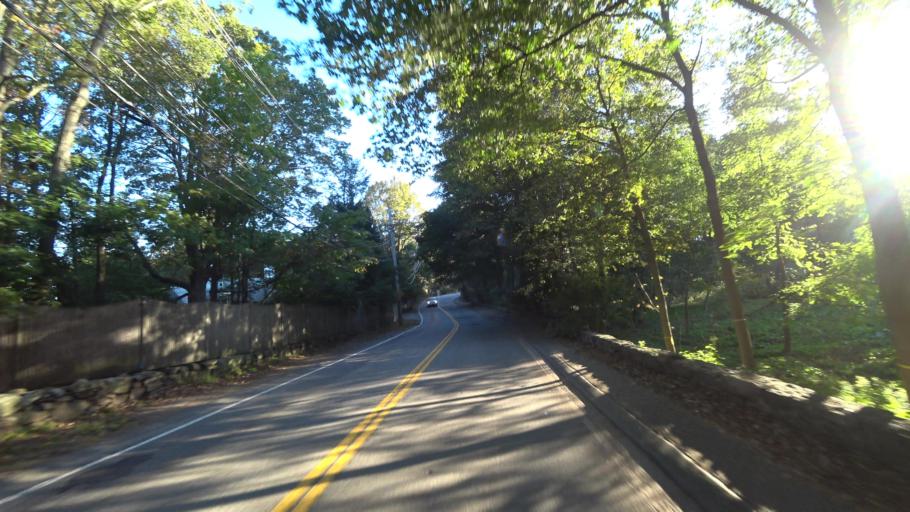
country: US
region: Massachusetts
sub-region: Norfolk County
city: Brookline
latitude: 42.3234
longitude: -71.1309
